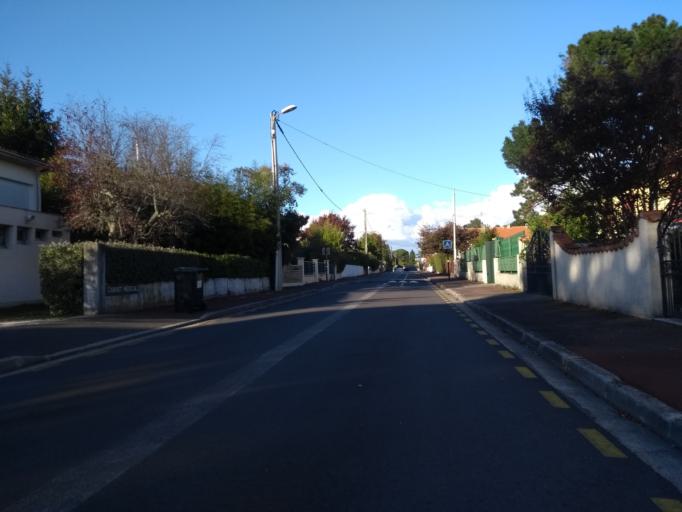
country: FR
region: Aquitaine
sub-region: Departement de la Gironde
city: Gradignan
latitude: 44.7723
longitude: -0.6117
